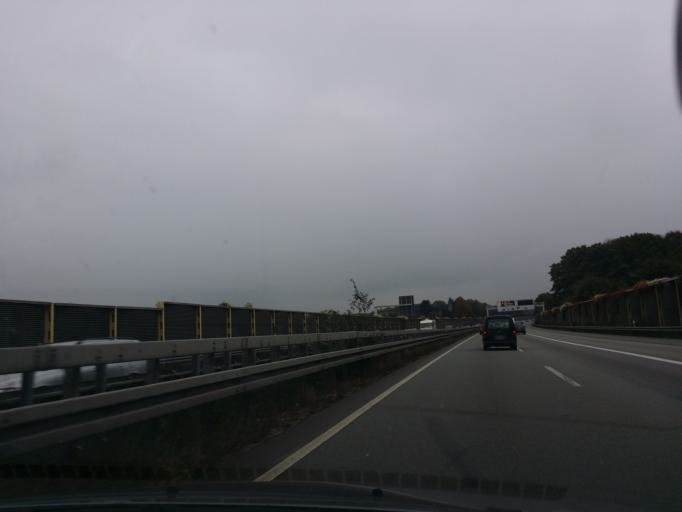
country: DE
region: North Rhine-Westphalia
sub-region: Regierungsbezirk Munster
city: Lotte
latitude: 52.2908
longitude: 7.9402
